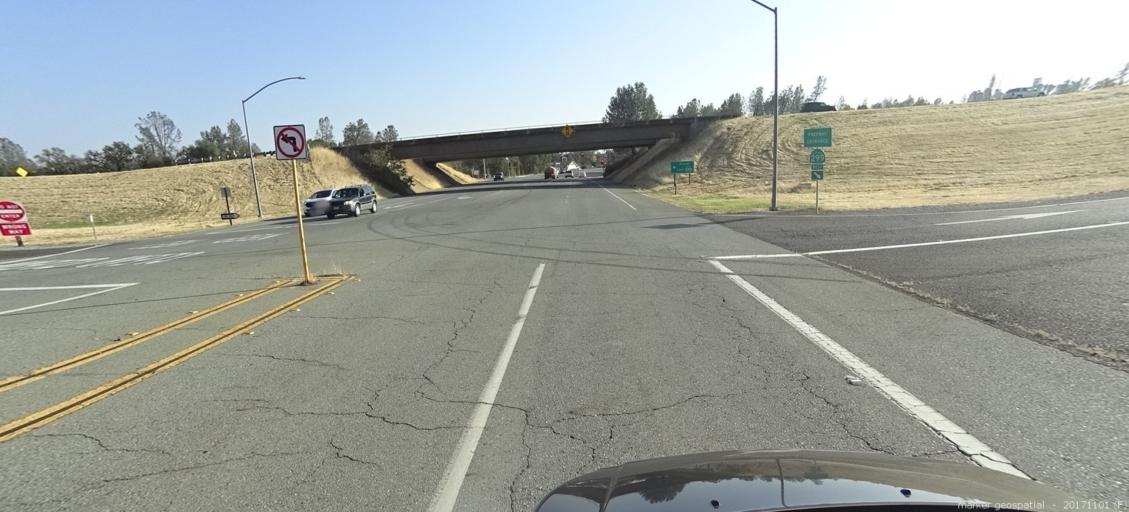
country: US
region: California
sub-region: Shasta County
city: Shasta Lake
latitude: 40.6216
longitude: -122.3191
